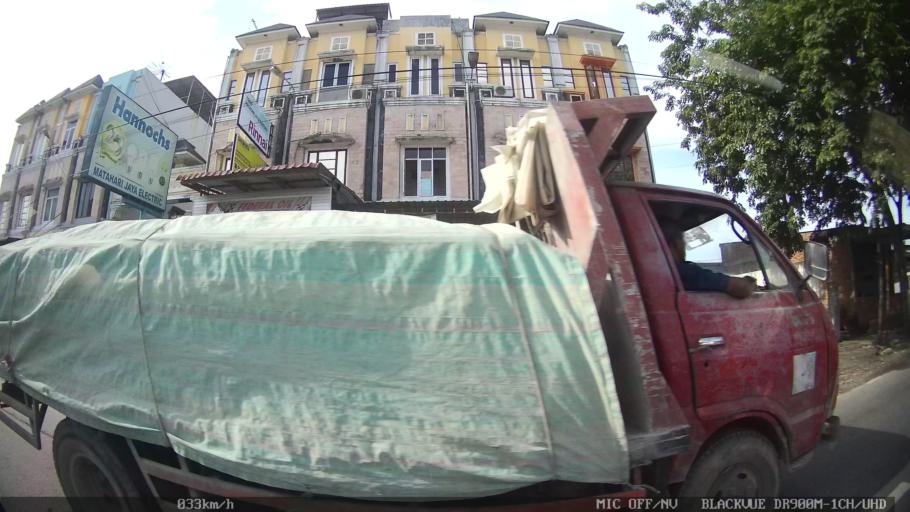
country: ID
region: North Sumatra
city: Medan
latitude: 3.6103
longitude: 98.6394
